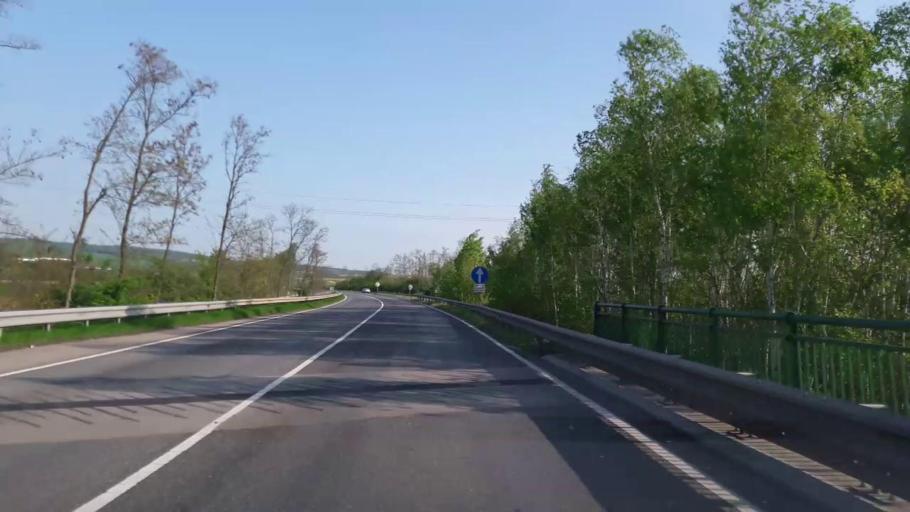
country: AT
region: Lower Austria
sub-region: Politischer Bezirk Hollabrunn
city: Hollabrunn
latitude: 48.5550
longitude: 16.0650
